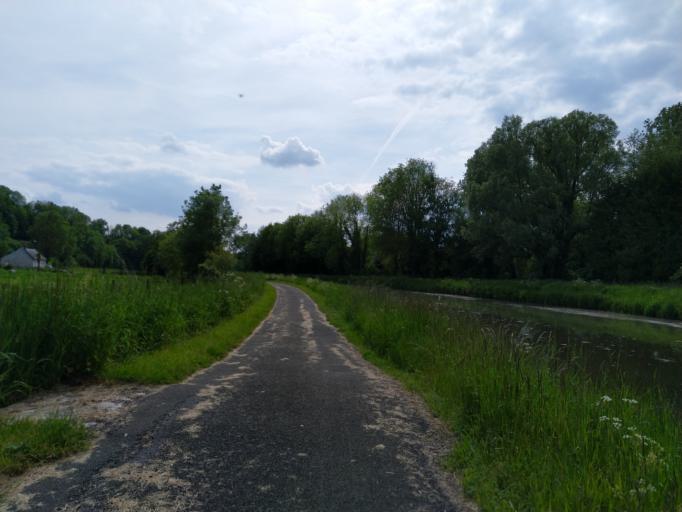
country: FR
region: Picardie
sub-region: Departement de l'Aisne
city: Etreux
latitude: 49.9698
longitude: 3.6253
